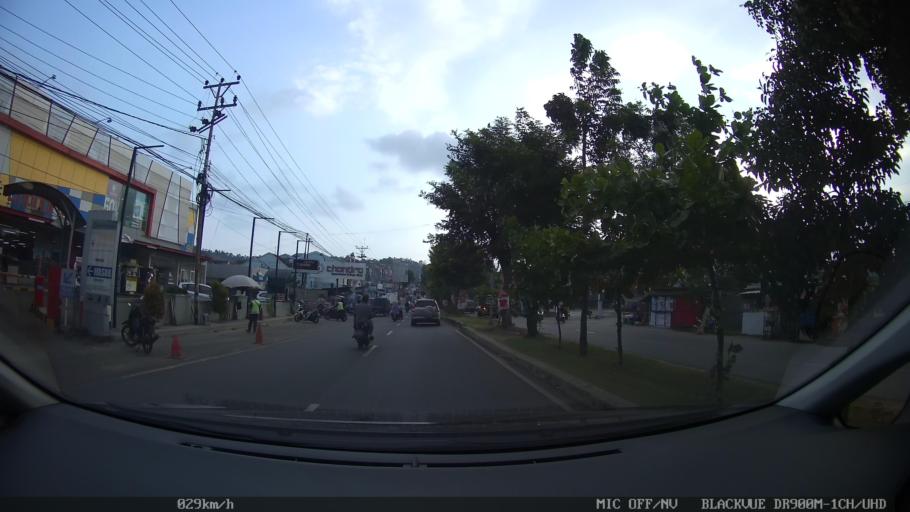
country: ID
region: Lampung
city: Kedaton
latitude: -5.3972
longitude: 105.2130
